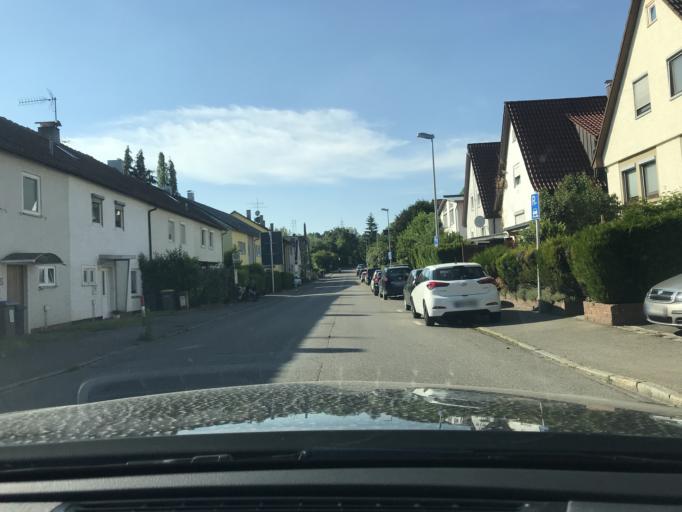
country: DE
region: Baden-Wuerttemberg
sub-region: Regierungsbezirk Stuttgart
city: Waiblingen
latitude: 48.8377
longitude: 9.3151
